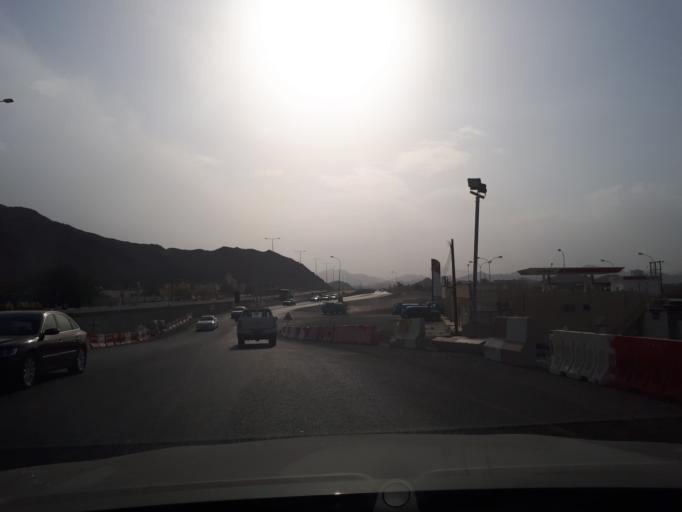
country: OM
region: Ash Sharqiyah
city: Ibra'
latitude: 22.8361
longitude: 58.4193
